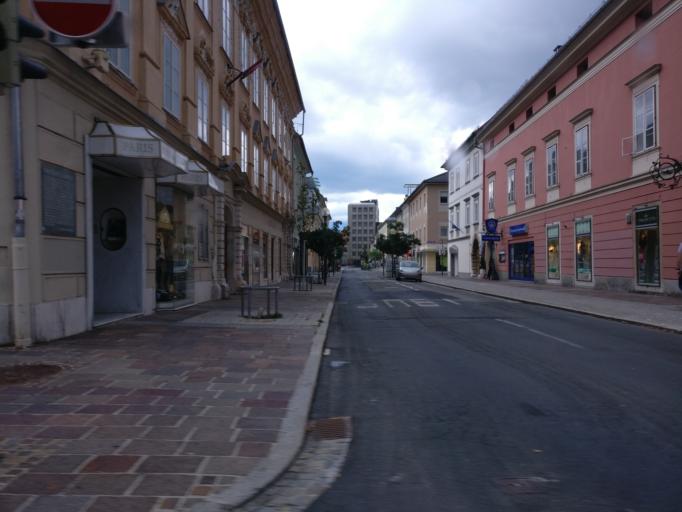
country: AT
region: Carinthia
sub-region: Klagenfurt am Woerthersee
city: Klagenfurt am Woerthersee
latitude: 46.6236
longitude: 14.3087
